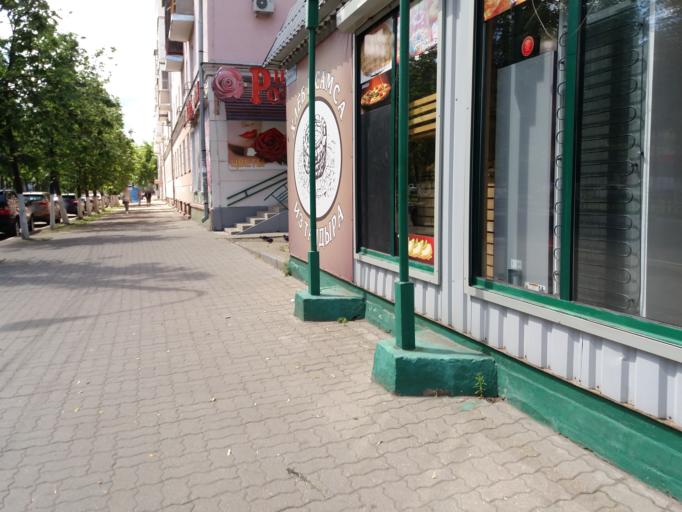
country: RU
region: Jaroslavl
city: Yaroslavl
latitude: 57.6322
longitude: 39.8555
